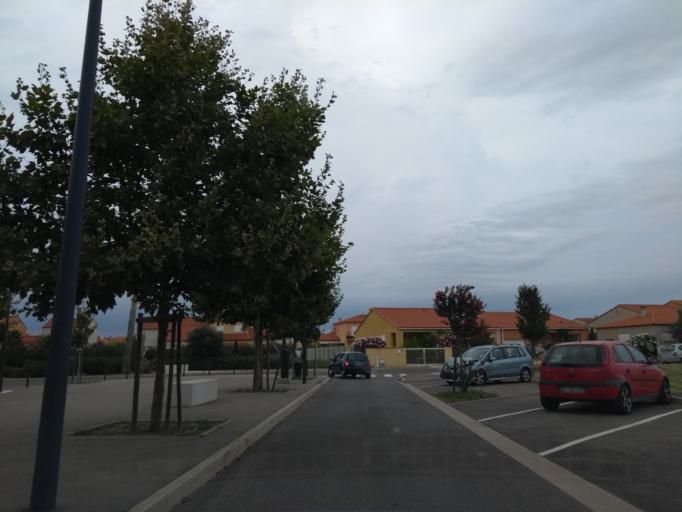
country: FR
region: Languedoc-Roussillon
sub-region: Departement des Pyrenees-Orientales
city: Elne
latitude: 42.6117
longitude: 2.9717
